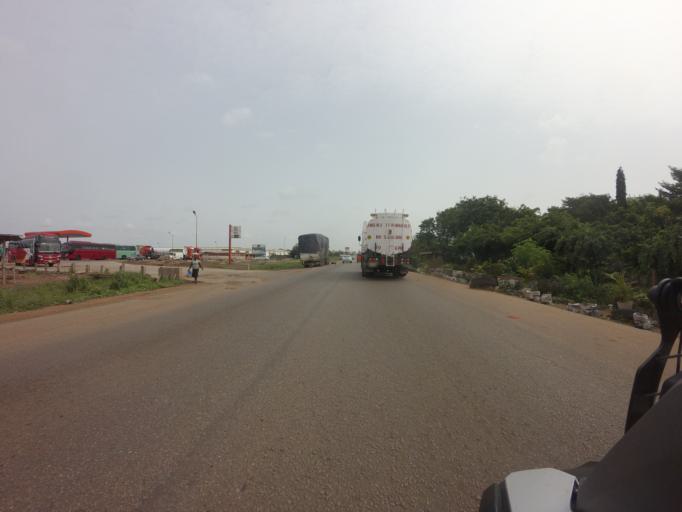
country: GH
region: Greater Accra
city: Tema
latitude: 5.7176
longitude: 0.0159
